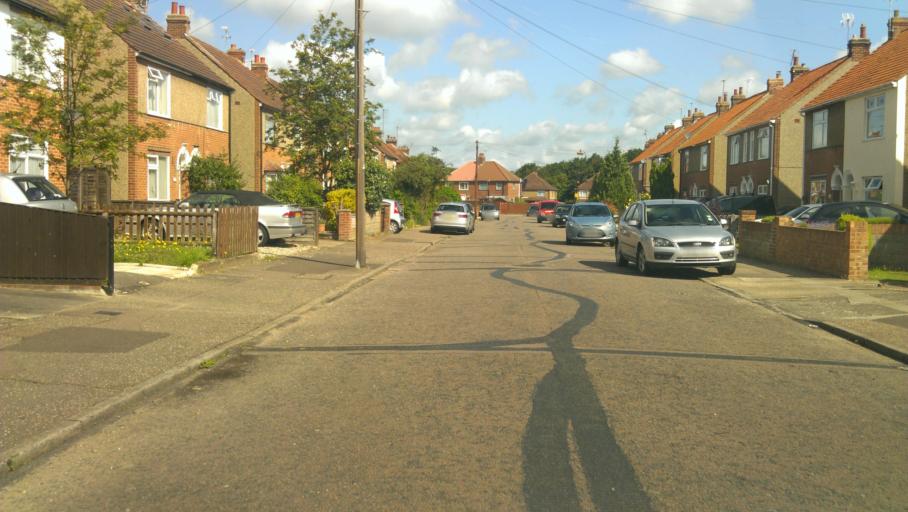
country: GB
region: England
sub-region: Essex
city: Colchester
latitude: 51.8738
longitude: 0.9199
